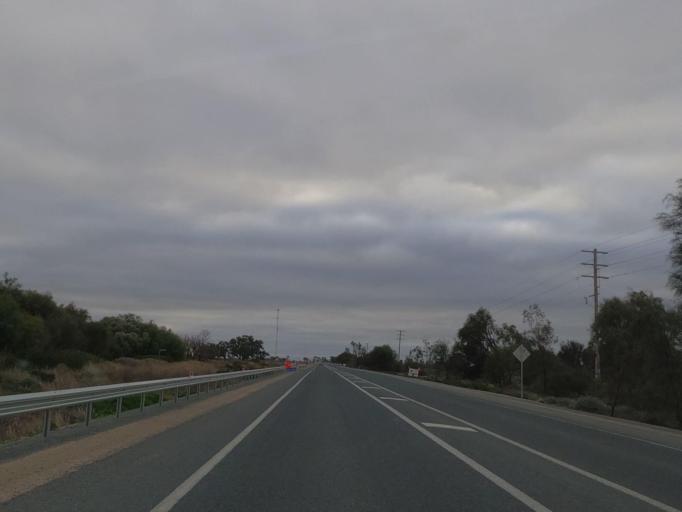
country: AU
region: Victoria
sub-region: Swan Hill
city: Swan Hill
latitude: -35.5349
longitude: 143.7443
